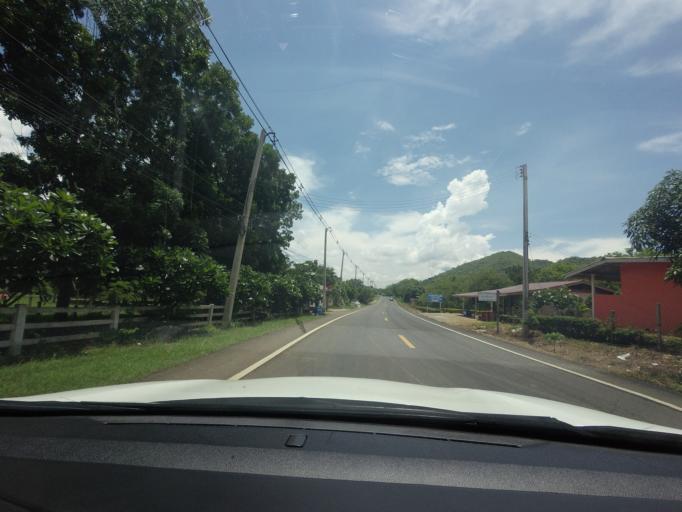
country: TH
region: Sara Buri
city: Muak Lek
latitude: 14.5862
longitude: 101.2424
